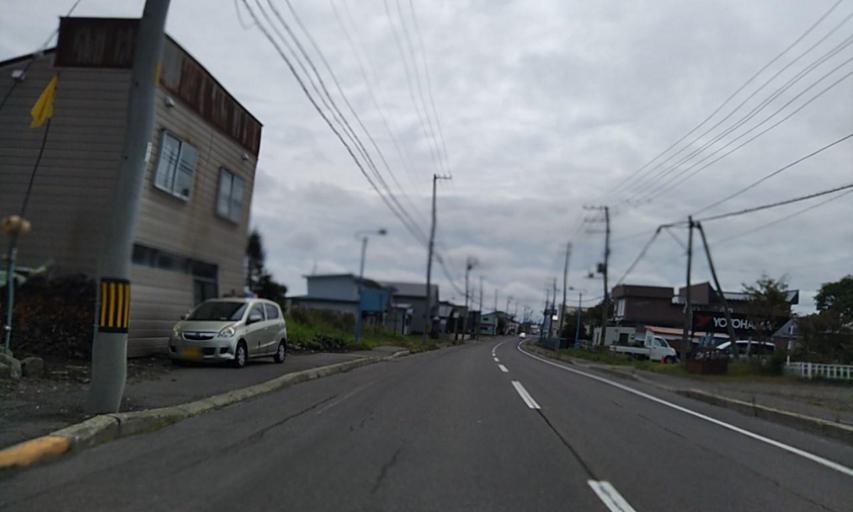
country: JP
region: Hokkaido
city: Shibetsu
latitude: 43.5727
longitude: 145.2183
